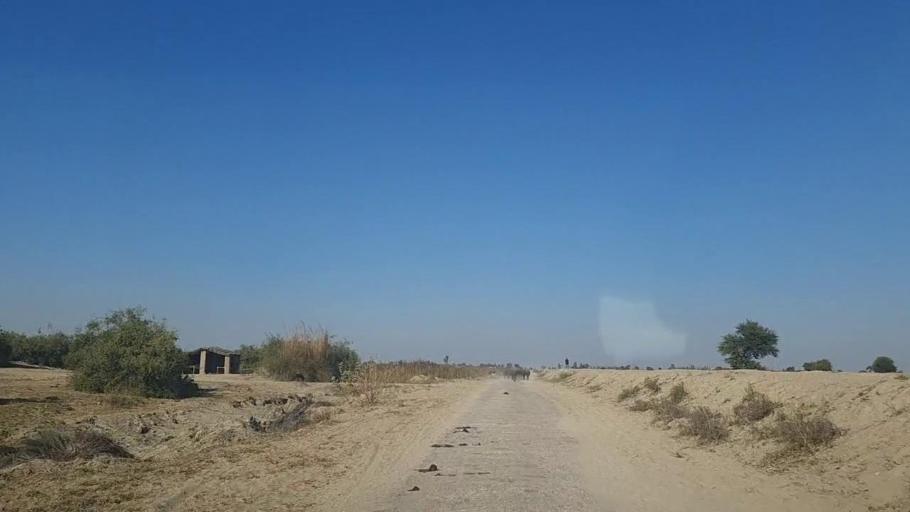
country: PK
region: Sindh
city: Sanghar
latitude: 26.2111
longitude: 68.9293
